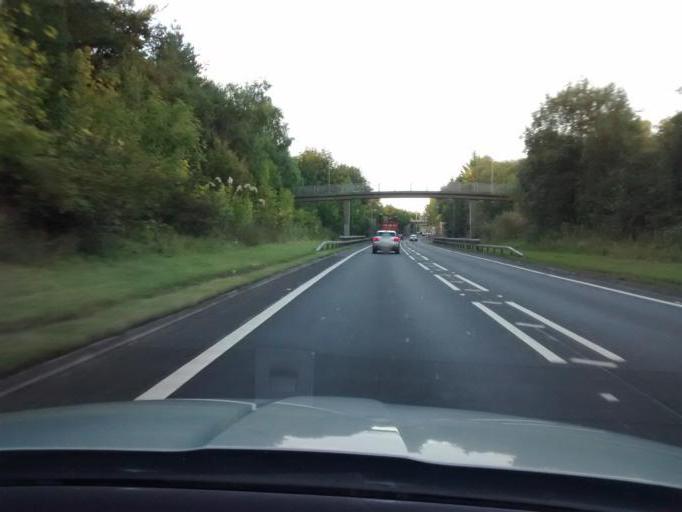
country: GB
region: Scotland
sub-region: Renfrewshire
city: Kilbarchan
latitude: 55.8279
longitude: -4.5385
